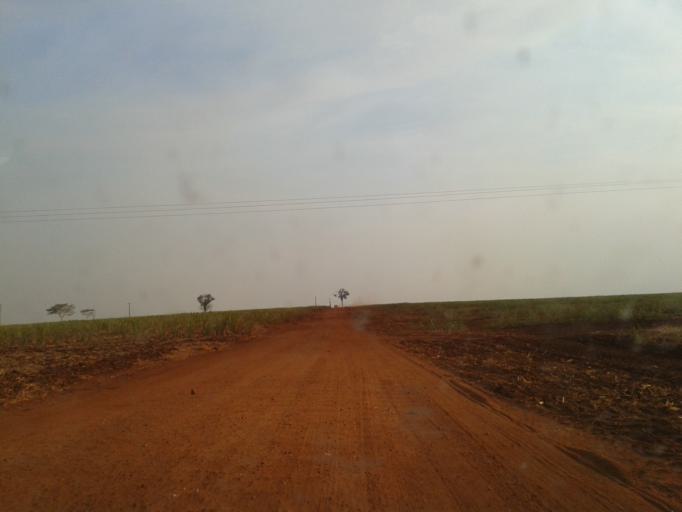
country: BR
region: Minas Gerais
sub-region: Capinopolis
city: Capinopolis
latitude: -18.7286
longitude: -49.6853
